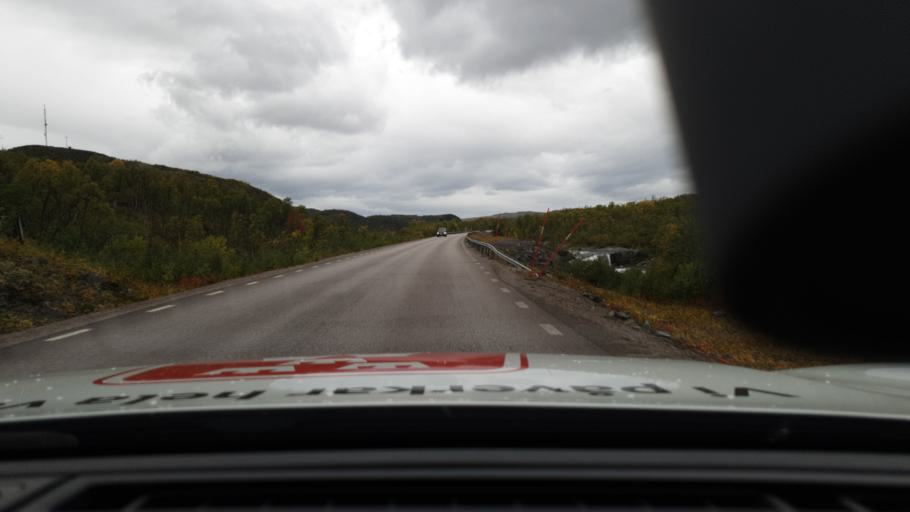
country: NO
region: Troms
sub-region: Bardu
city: Setermoen
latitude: 68.4337
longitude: 18.6569
